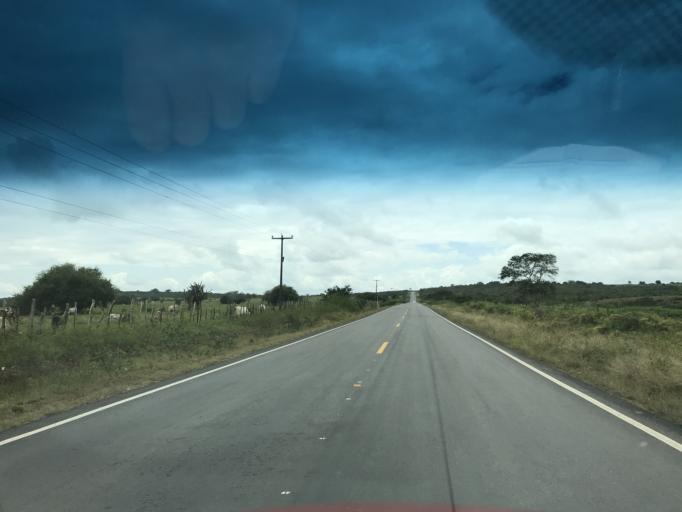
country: BR
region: Bahia
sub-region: Conceicao Do Almeida
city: Conceicao do Almeida
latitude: -12.6729
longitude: -39.2927
